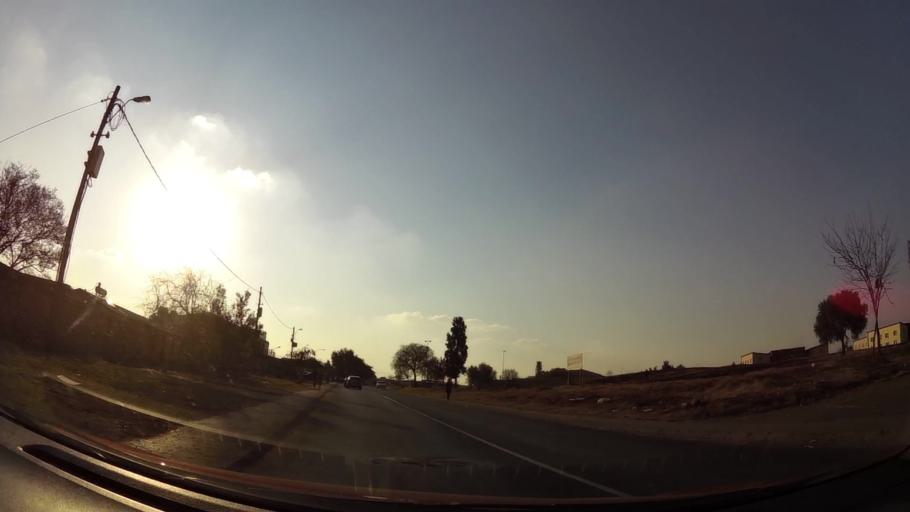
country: ZA
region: Gauteng
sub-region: City of Johannesburg Metropolitan Municipality
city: Soweto
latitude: -26.2934
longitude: 27.8959
